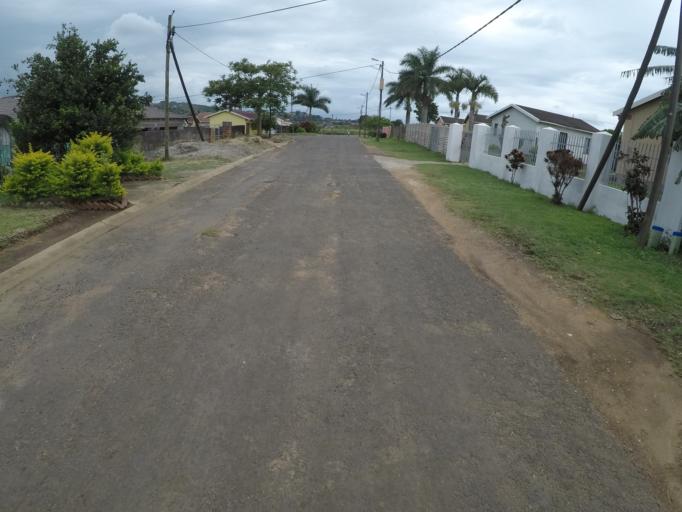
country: ZA
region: KwaZulu-Natal
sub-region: uThungulu District Municipality
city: Empangeni
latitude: -28.7836
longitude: 31.8536
